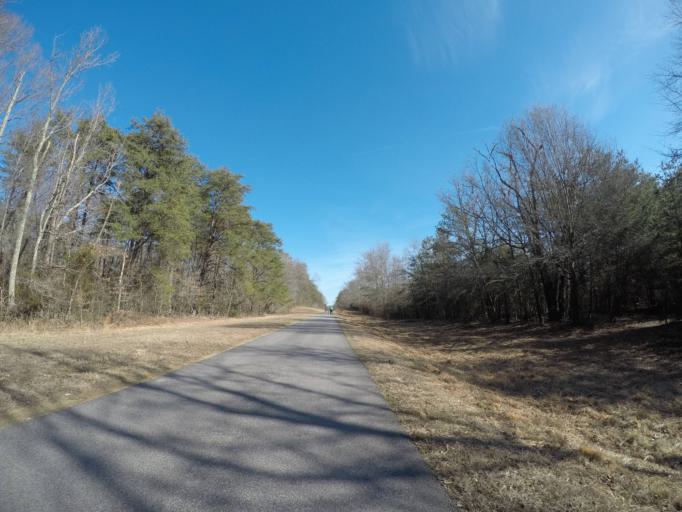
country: US
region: Maryland
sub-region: Charles County
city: Saint Charles
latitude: 38.5967
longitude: -76.9679
